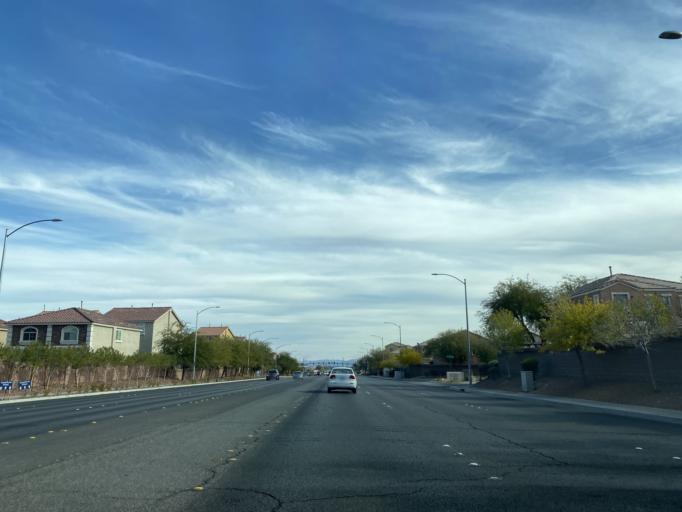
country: US
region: Nevada
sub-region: Clark County
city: Enterprise
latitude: 36.0562
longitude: -115.2293
